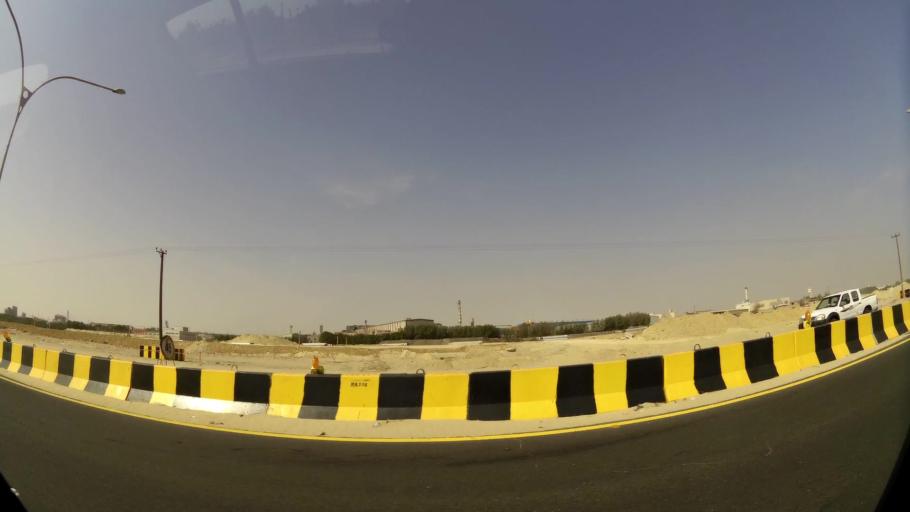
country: KW
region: Al Ahmadi
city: Al Fahahil
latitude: 28.9867
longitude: 48.1373
